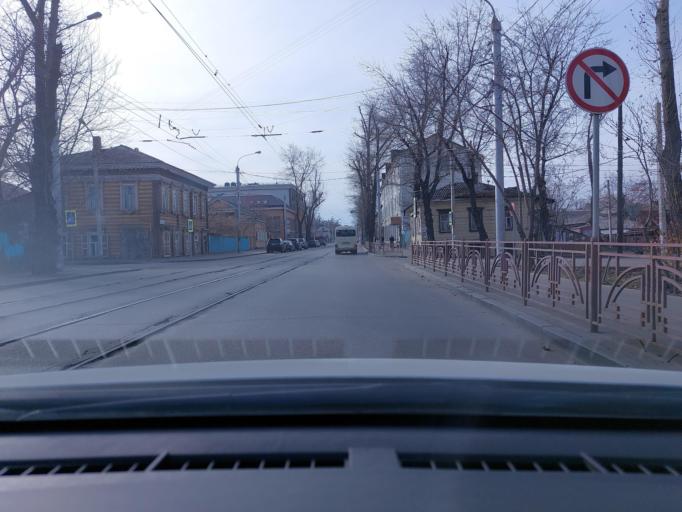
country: RU
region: Irkutsk
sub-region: Irkutskiy Rayon
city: Irkutsk
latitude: 52.2789
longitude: 104.2921
